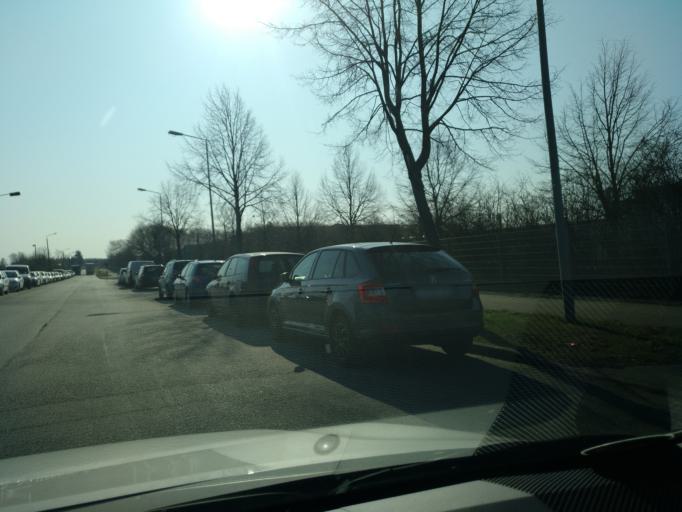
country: DE
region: Berlin
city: Mahlsdorf
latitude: 52.5078
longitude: 13.6404
